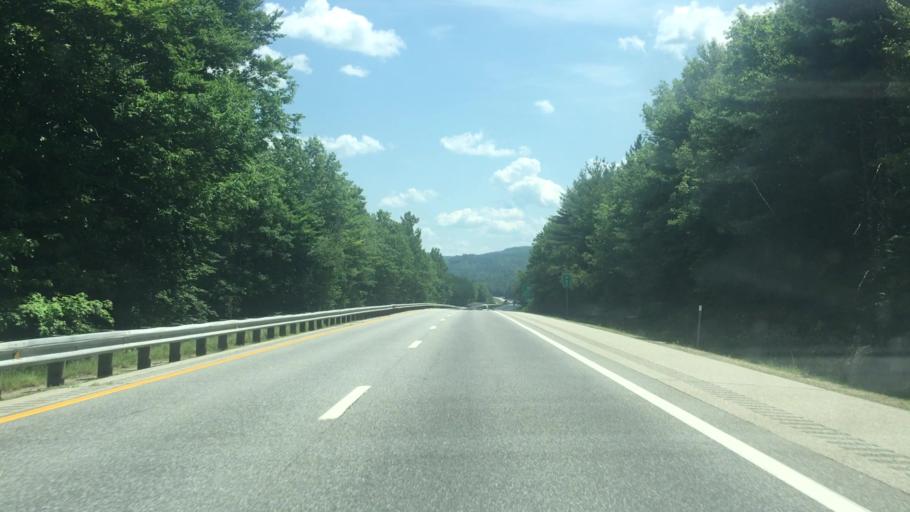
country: US
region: New Hampshire
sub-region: Merrimack County
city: Sutton
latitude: 43.3008
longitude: -71.8414
